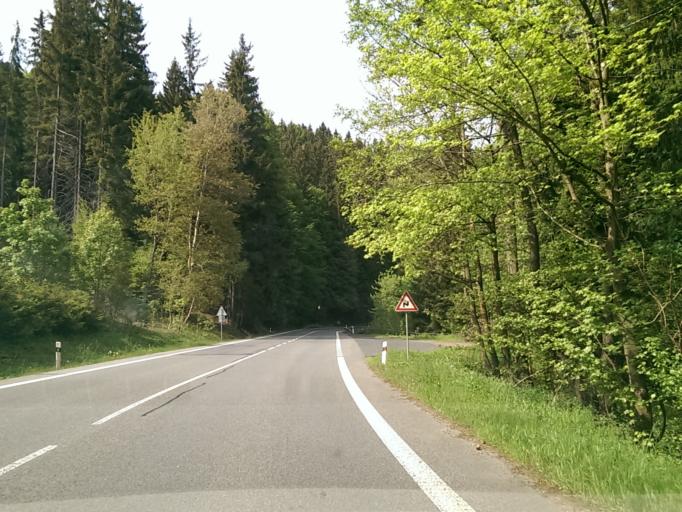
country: CZ
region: Liberecky
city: Zelezny Brod
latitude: 50.6677
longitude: 15.2617
